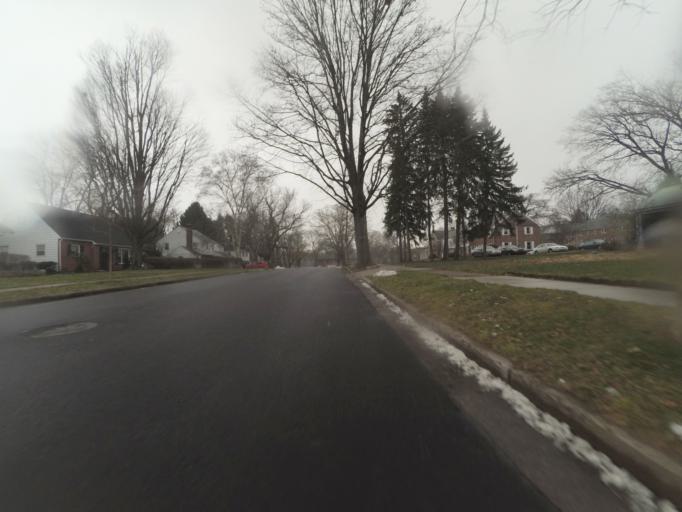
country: US
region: Pennsylvania
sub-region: Centre County
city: State College
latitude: 40.7905
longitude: -77.8492
